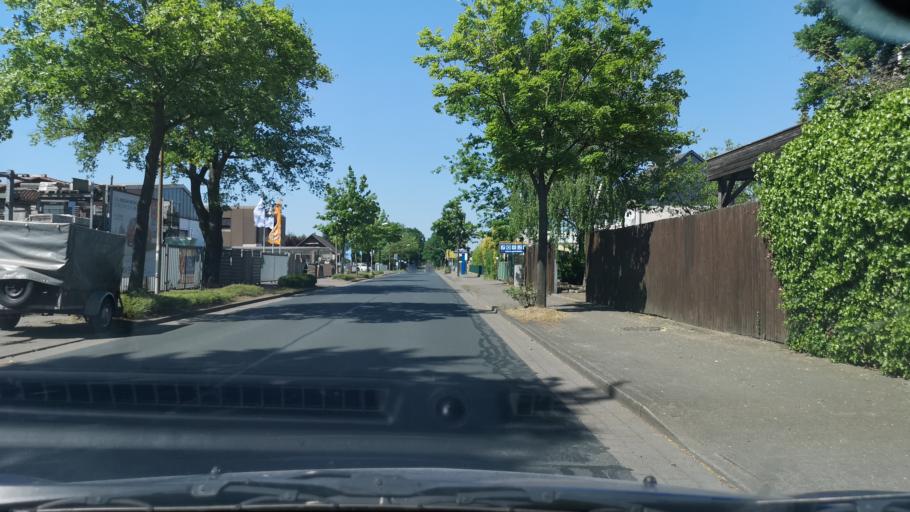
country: DE
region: Lower Saxony
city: Garbsen-Mitte
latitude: 52.4448
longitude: 9.6085
